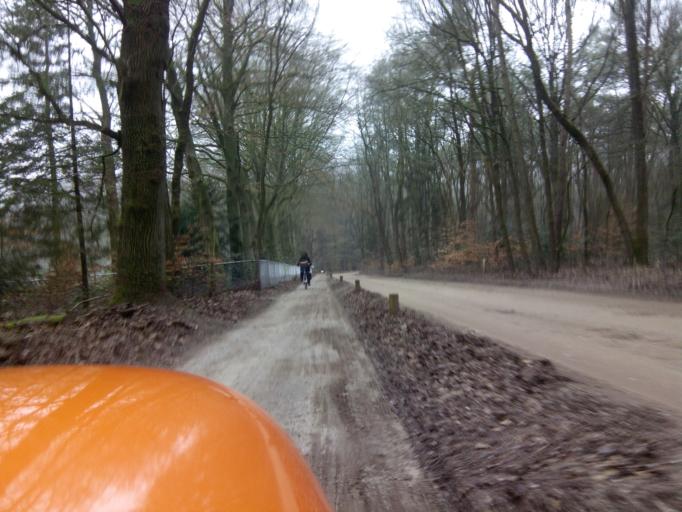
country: NL
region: Gelderland
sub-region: Gemeente Barneveld
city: Stroe
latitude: 52.2189
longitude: 5.6585
